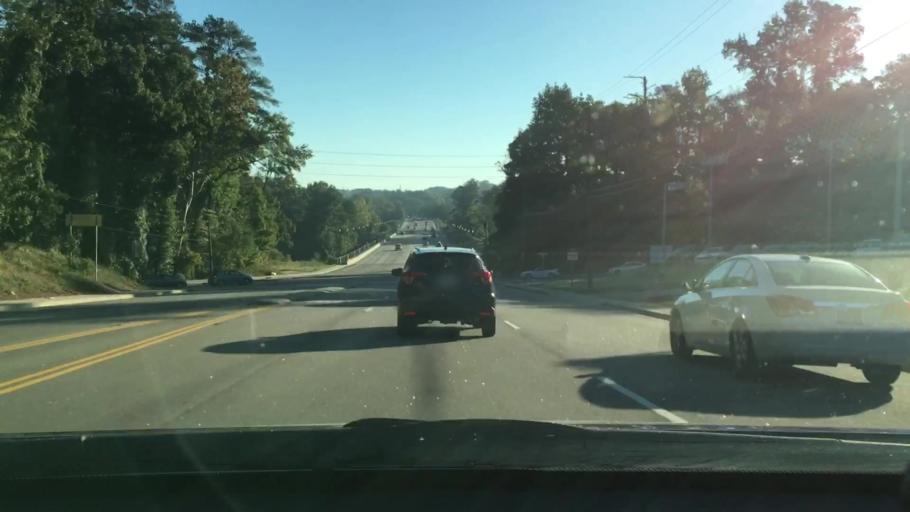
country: US
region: South Carolina
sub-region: Lexington County
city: West Columbia
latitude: 34.0254
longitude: -81.0726
